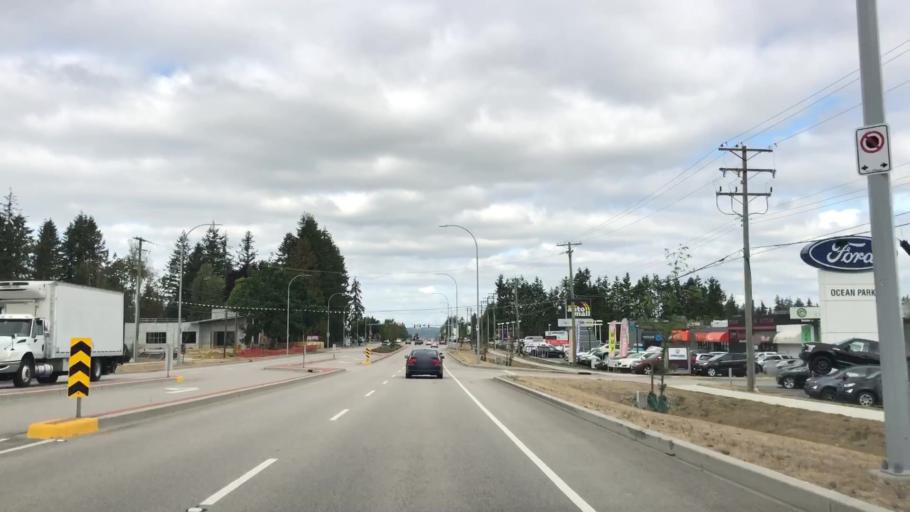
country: CA
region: British Columbia
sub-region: Greater Vancouver Regional District
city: White Rock
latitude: 49.0567
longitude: -122.8071
